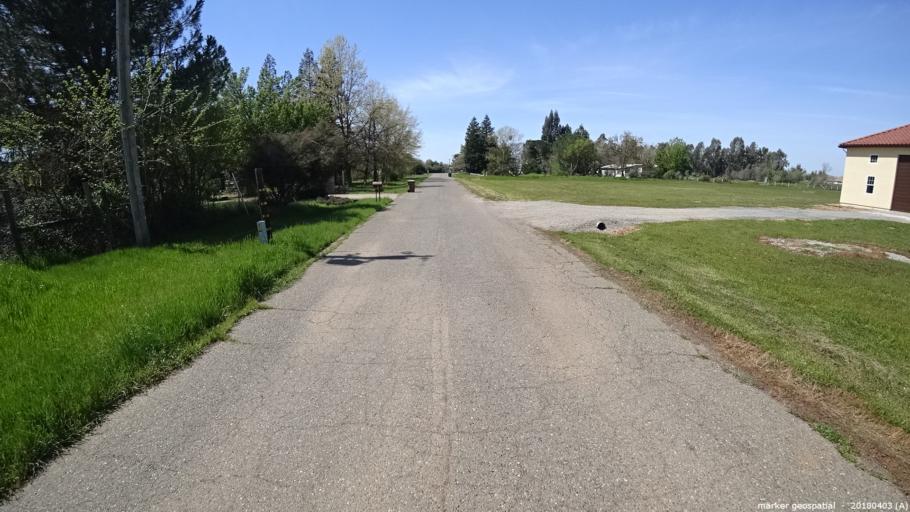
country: US
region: California
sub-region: Sacramento County
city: Wilton
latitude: 38.3833
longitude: -121.2482
